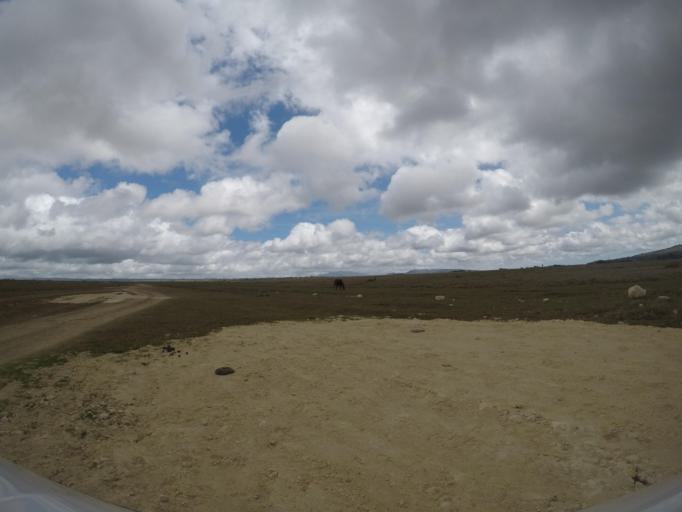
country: TL
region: Lautem
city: Lospalos
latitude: -8.4494
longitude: 126.9867
